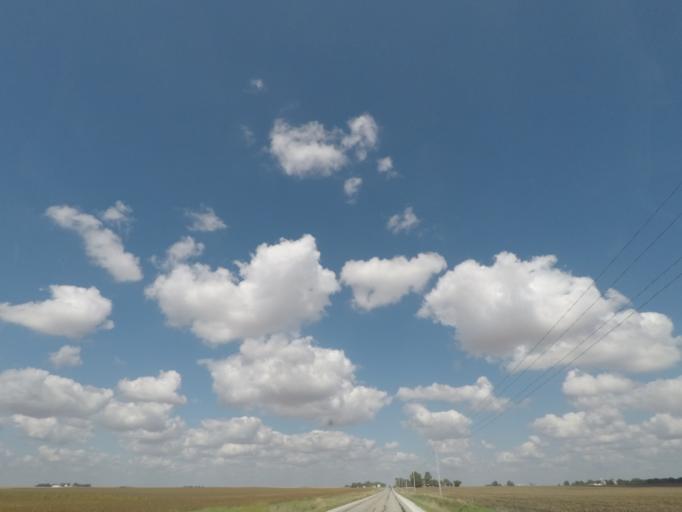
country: US
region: Iowa
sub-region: Story County
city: Nevada
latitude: 42.0565
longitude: -93.4057
